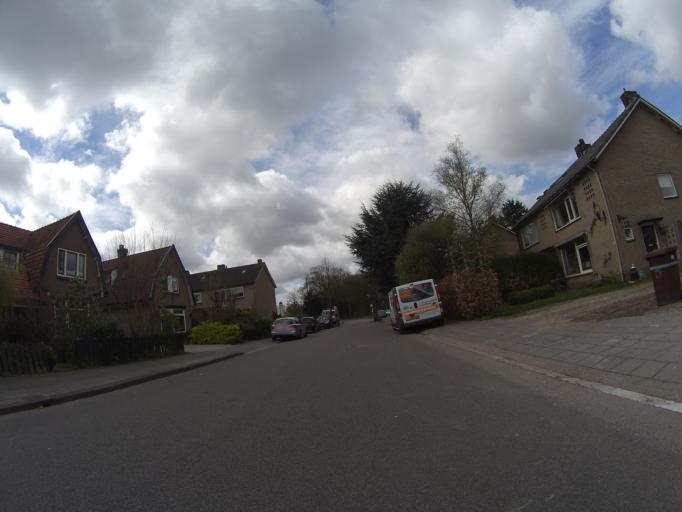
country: NL
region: Utrecht
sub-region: Gemeente Soest
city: Soest
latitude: 52.1839
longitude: 5.2699
